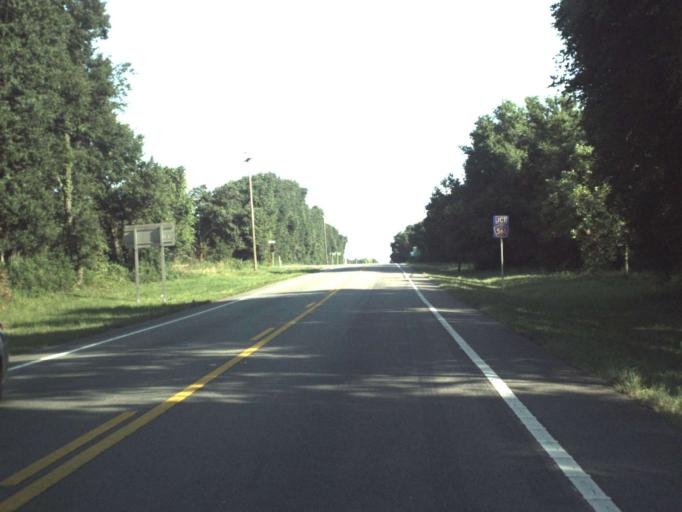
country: US
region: Florida
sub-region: Lake County
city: Groveland
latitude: 28.4108
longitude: -81.8305
